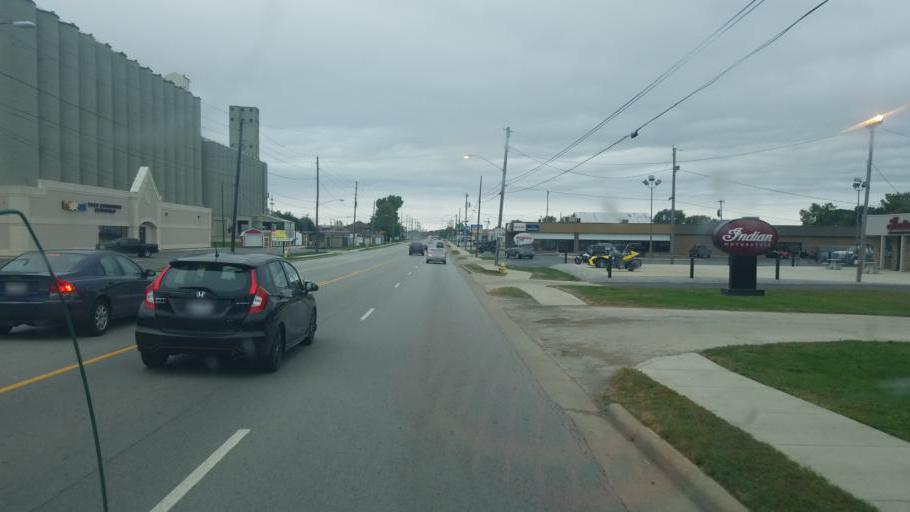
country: US
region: Ohio
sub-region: Lucas County
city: Maumee
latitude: 41.5699
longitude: -83.6576
